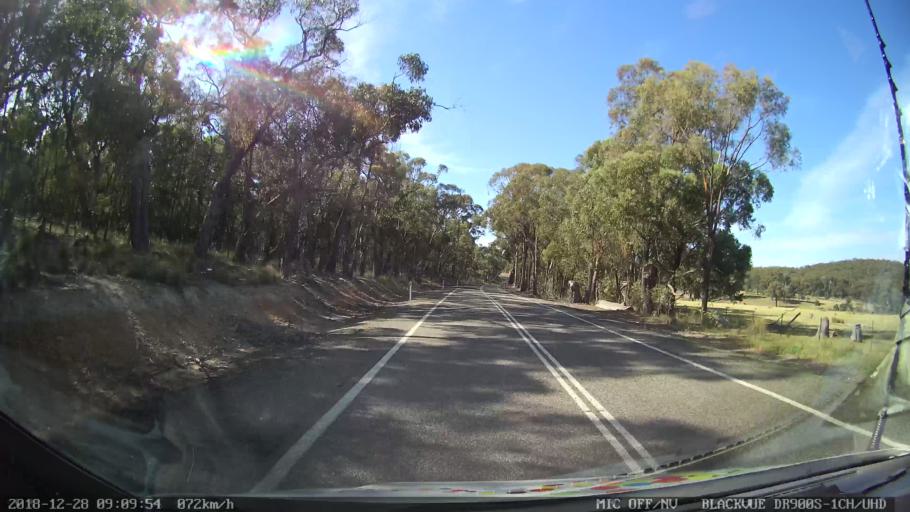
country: AU
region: New South Wales
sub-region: Upper Lachlan Shire
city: Crookwell
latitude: -34.2261
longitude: 149.3359
